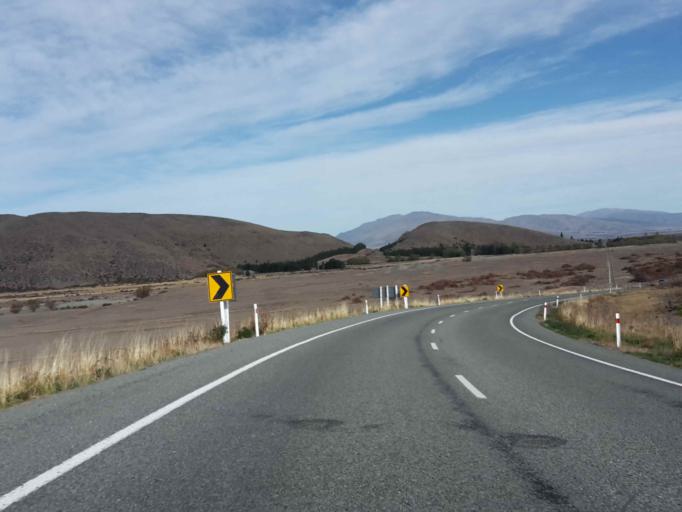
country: NZ
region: Canterbury
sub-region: Timaru District
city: Pleasant Point
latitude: -44.0419
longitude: 170.5080
